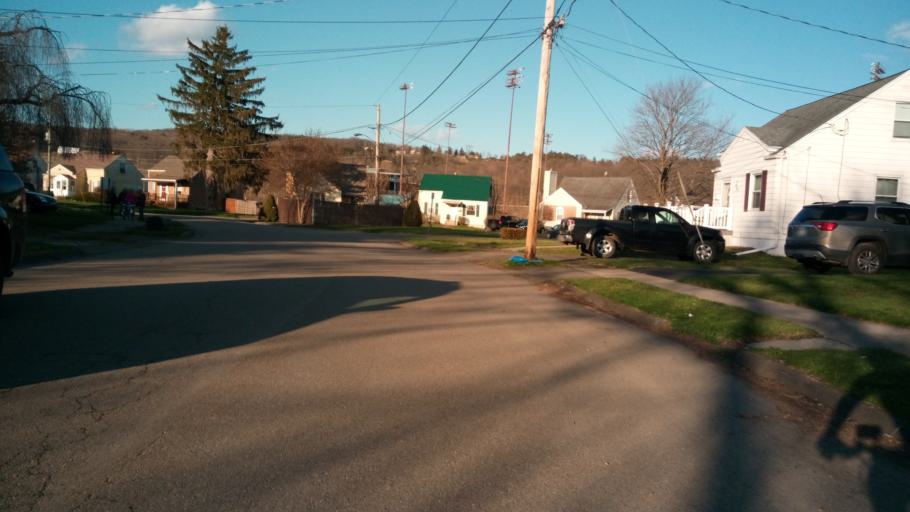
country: US
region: New York
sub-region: Chemung County
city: Elmira
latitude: 42.0792
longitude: -76.7829
